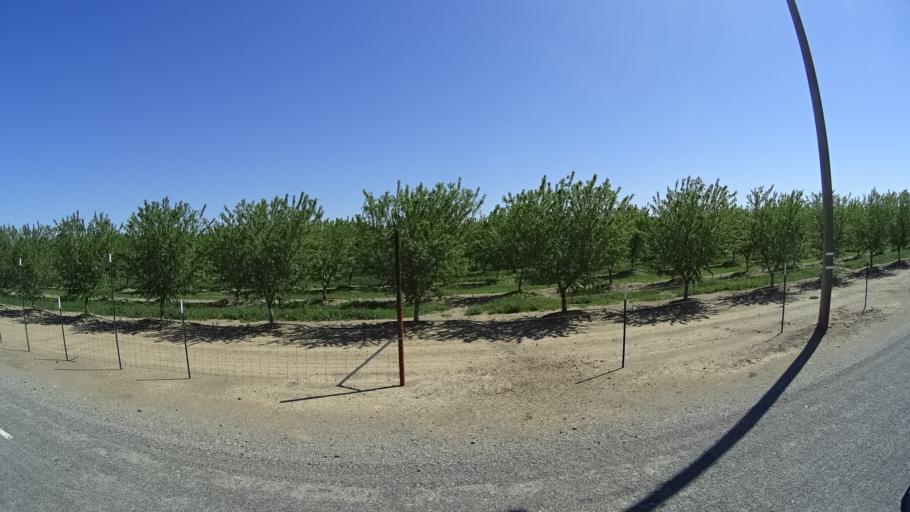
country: US
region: California
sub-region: Glenn County
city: Orland
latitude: 39.6951
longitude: -122.2340
